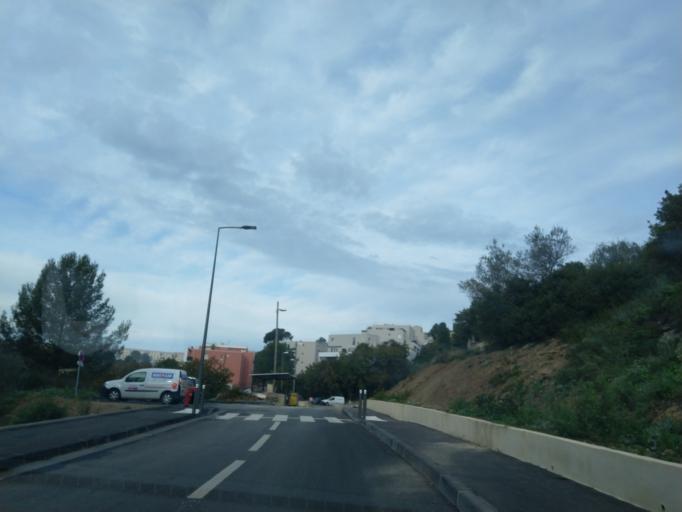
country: FR
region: Provence-Alpes-Cote d'Azur
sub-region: Departement des Bouches-du-Rhone
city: Marseille 12
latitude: 43.2982
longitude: 5.4443
